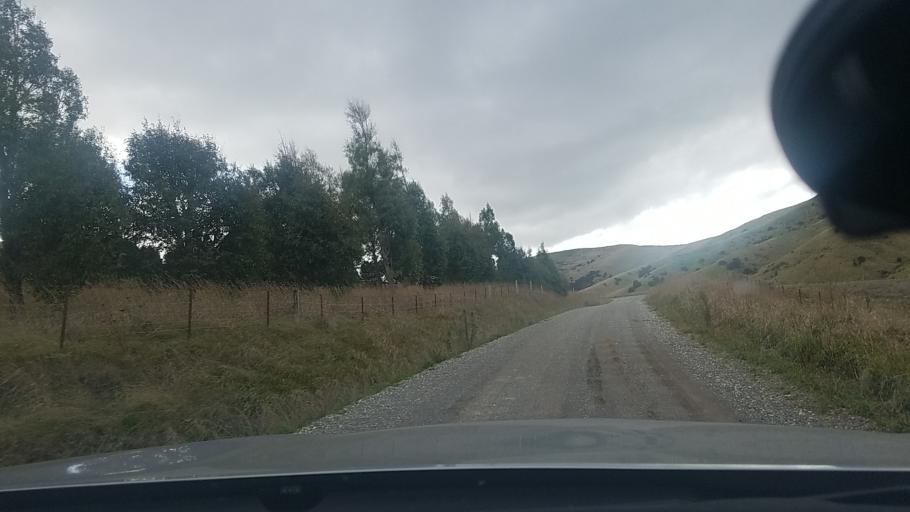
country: NZ
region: Marlborough
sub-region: Marlborough District
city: Blenheim
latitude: -41.5895
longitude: 174.0928
